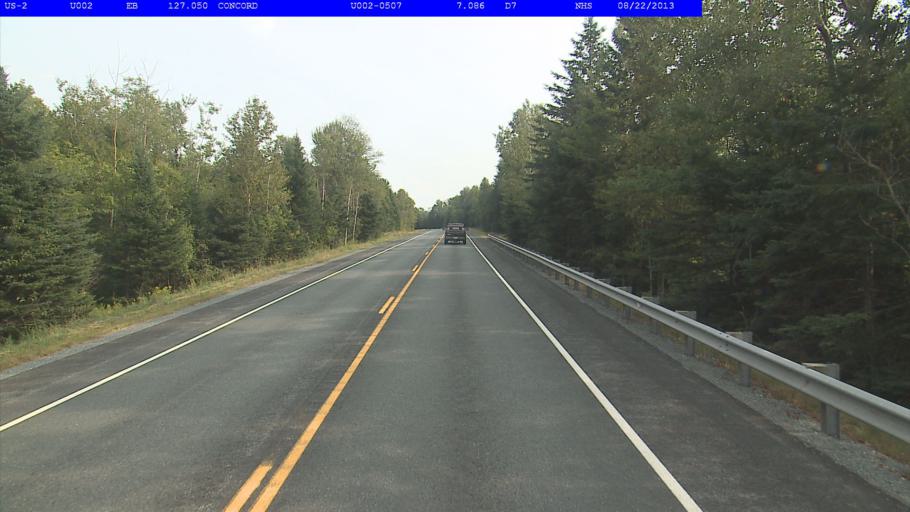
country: US
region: New Hampshire
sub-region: Grafton County
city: Littleton
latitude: 44.4580
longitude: -71.8310
